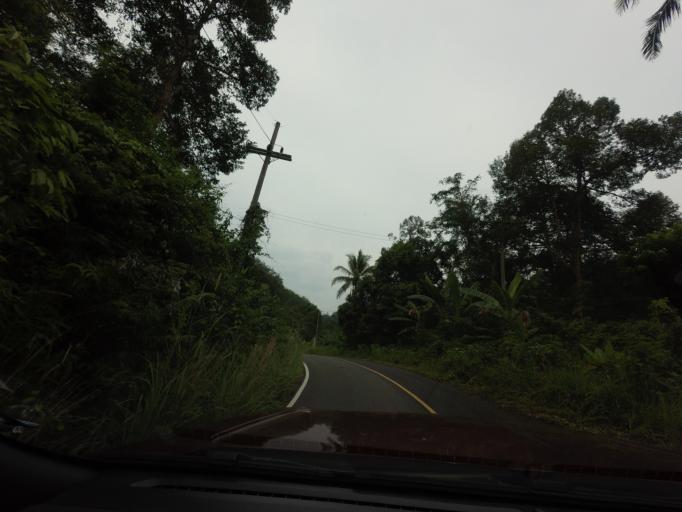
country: TH
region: Narathiwat
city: Si Sakhon
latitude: 6.0633
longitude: 101.3846
